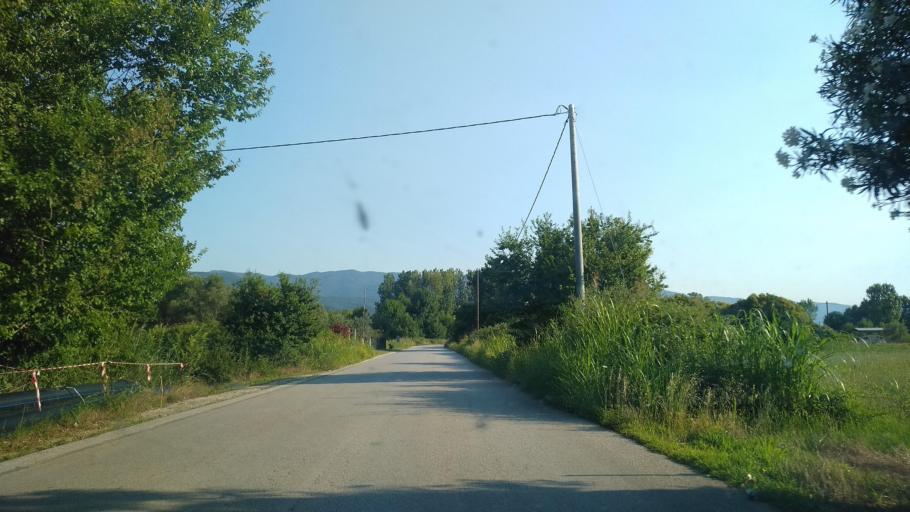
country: GR
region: Central Macedonia
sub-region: Nomos Thessalonikis
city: Stavros
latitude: 40.6792
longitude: 23.6868
